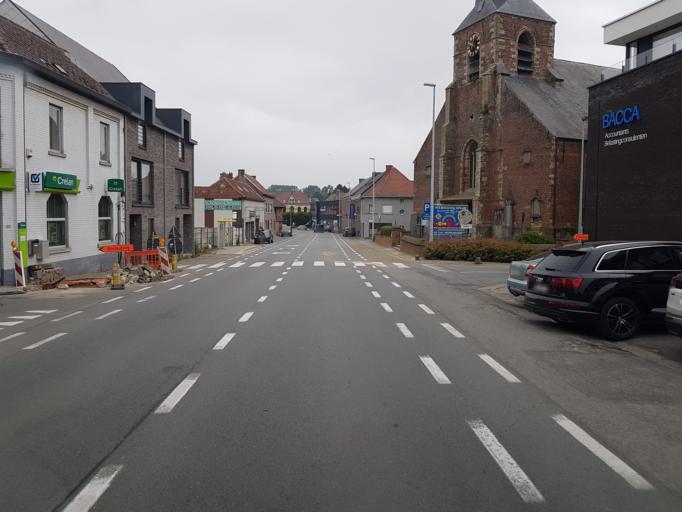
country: BE
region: Flanders
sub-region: Provincie Oost-Vlaanderen
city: Ninove
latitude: 50.8415
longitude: 3.9568
